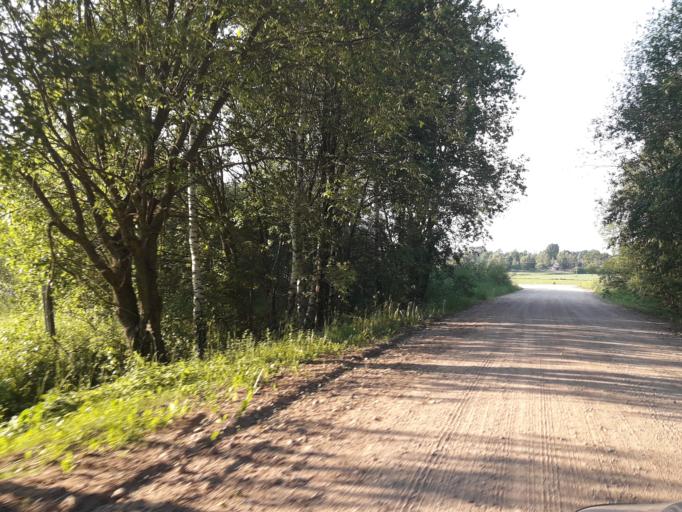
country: BY
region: Minsk
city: Pyatryshki
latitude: 54.1340
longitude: 27.1426
